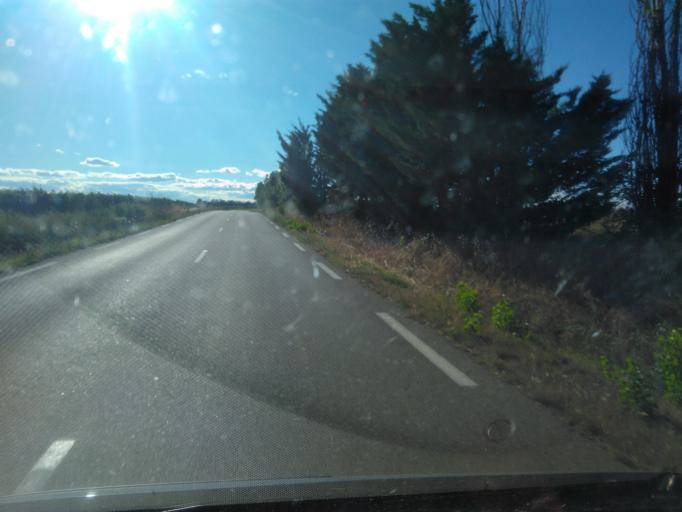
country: FR
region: Languedoc-Roussillon
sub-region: Departement du Gard
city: Vauvert
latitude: 43.6511
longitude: 4.3125
